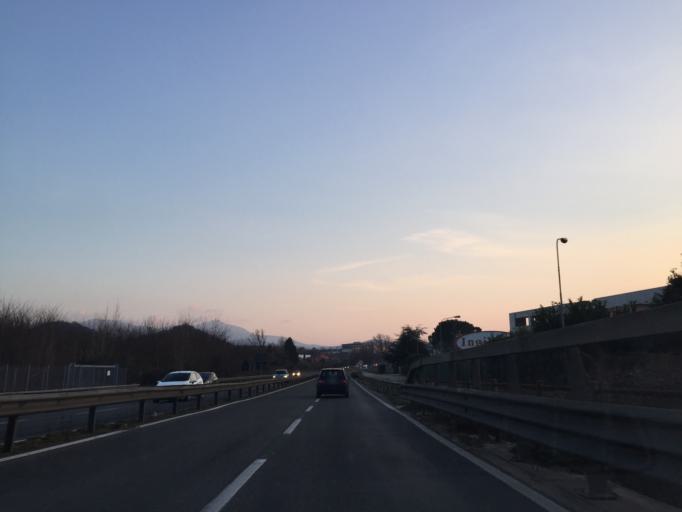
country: IT
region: Campania
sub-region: Provincia di Avellino
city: Atripalda
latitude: 40.9315
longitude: 14.8307
